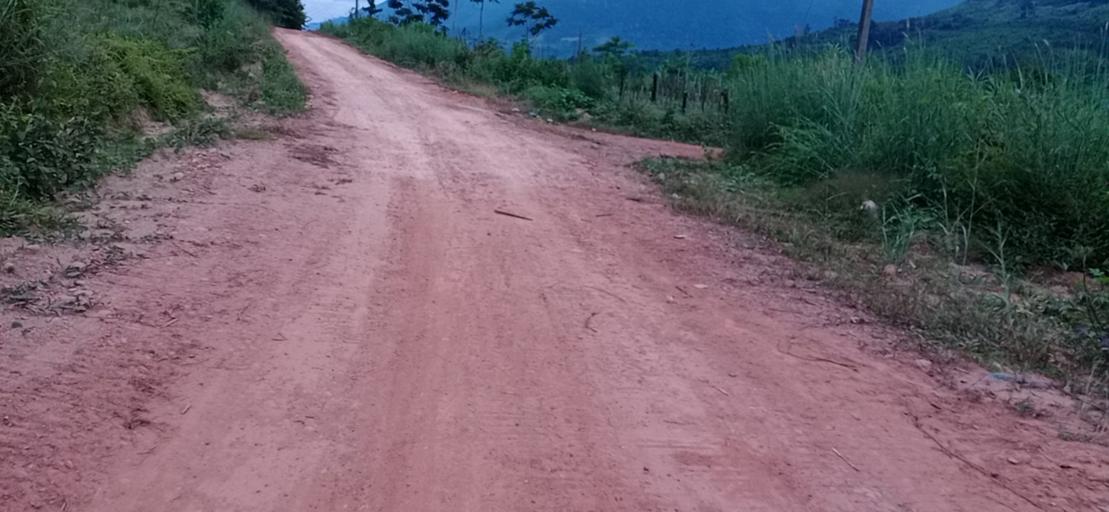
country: TH
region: Changwat Bueng Kan
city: Pak Khat
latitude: 18.5526
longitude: 103.1658
